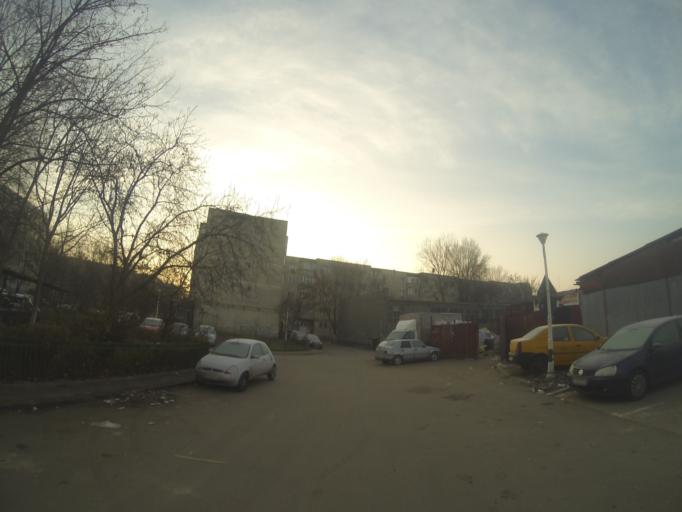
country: RO
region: Bucuresti
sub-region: Municipiul Bucuresti
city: Bucuresti
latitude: 44.4069
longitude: 26.0741
